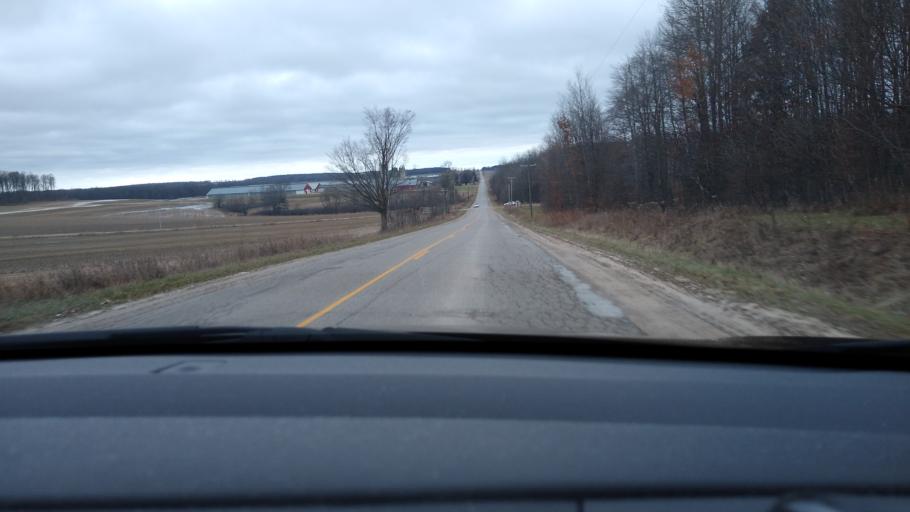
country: US
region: Michigan
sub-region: Missaukee County
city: Lake City
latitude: 44.2910
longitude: -85.0542
